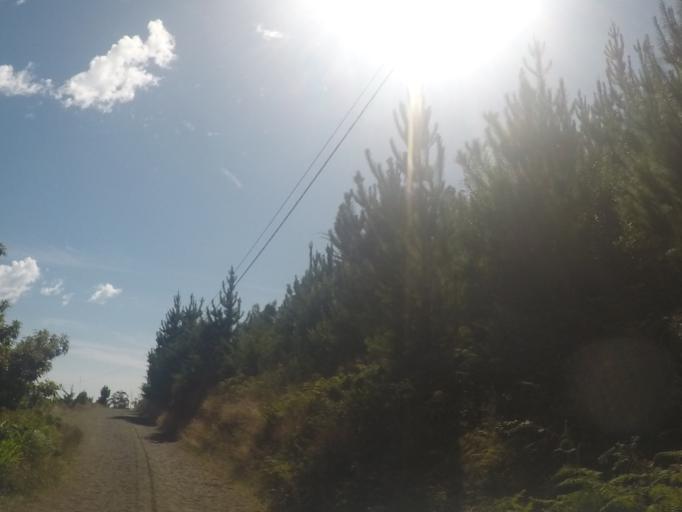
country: PT
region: Madeira
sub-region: Funchal
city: Nossa Senhora do Monte
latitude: 32.6985
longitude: -16.9044
